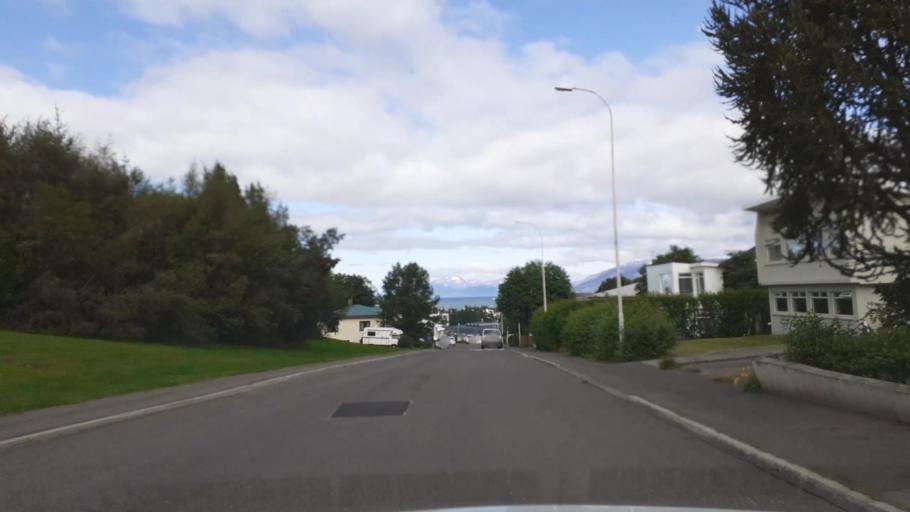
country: IS
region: Northeast
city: Akureyri
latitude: 65.6827
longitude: -18.1035
